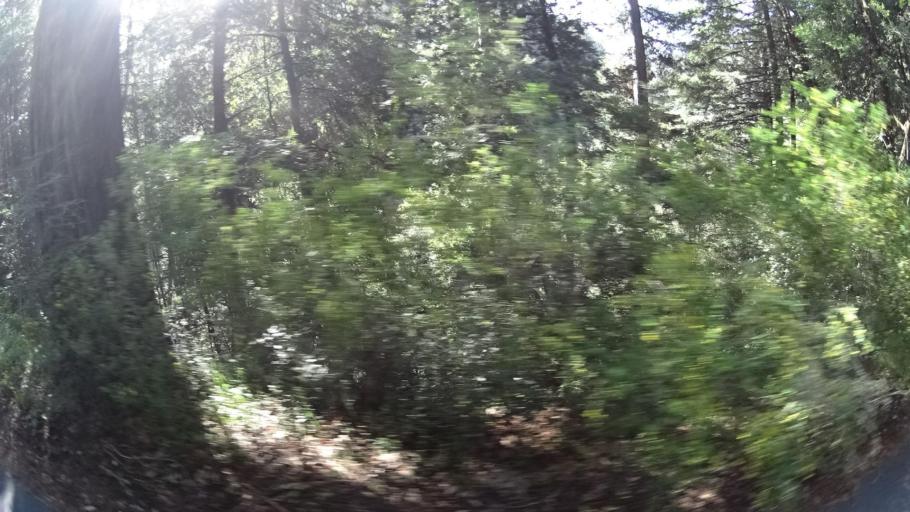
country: US
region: California
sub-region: Humboldt County
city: Rio Dell
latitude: 40.3433
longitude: -123.9403
